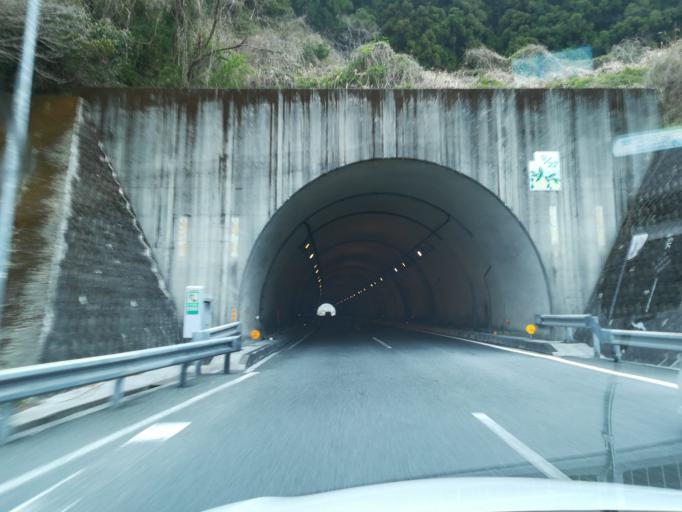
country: JP
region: Kochi
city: Kochi-shi
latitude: 33.7735
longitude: 133.6606
